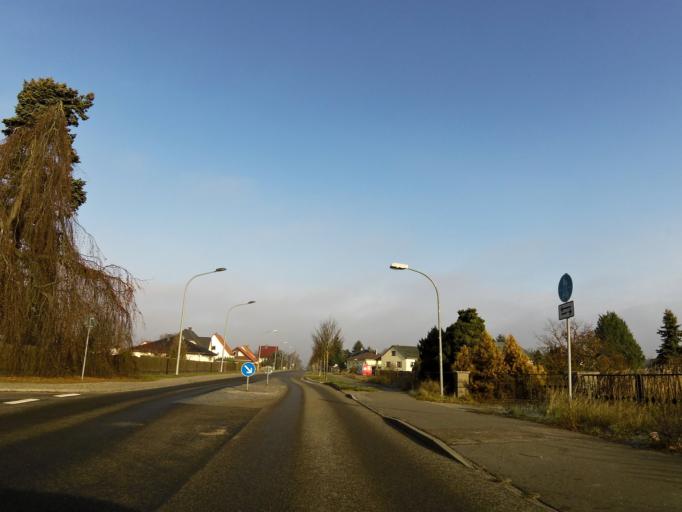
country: DE
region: Brandenburg
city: Werder
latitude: 52.3483
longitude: 12.9029
